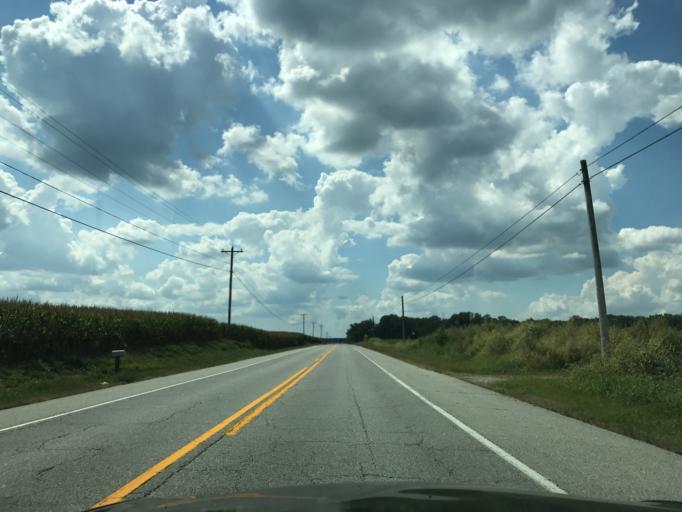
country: US
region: Maryland
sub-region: Queen Anne's County
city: Kingstown
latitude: 39.1822
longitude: -75.9003
